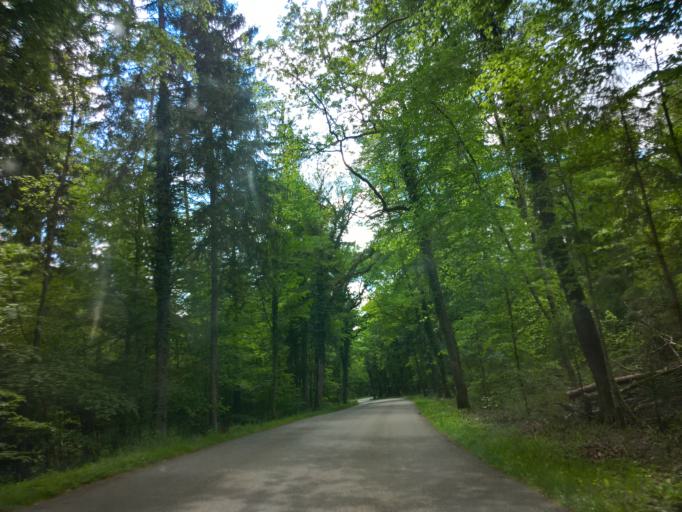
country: CH
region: Zurich
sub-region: Bezirk Andelfingen
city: Marthalen
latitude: 47.6099
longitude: 8.6126
